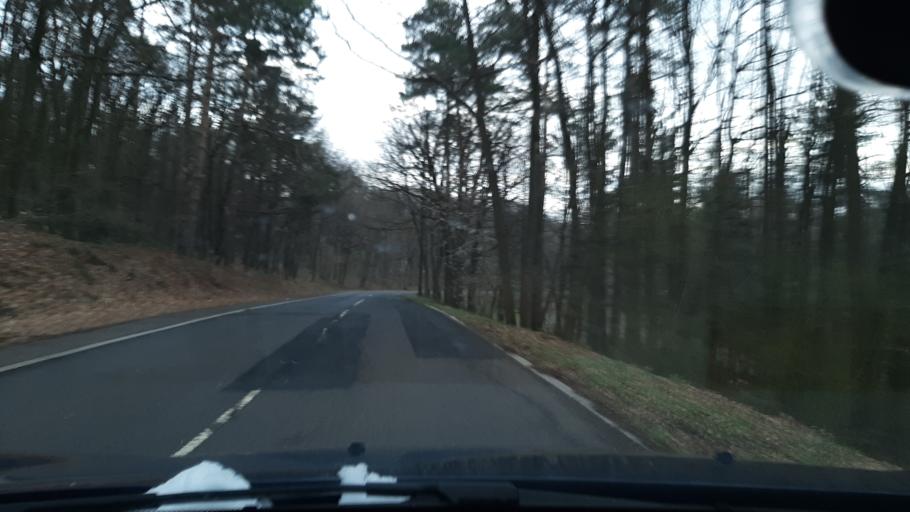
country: DE
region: North Rhine-Westphalia
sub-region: Regierungsbezirk Koln
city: Mechernich
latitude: 50.6047
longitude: 6.6757
